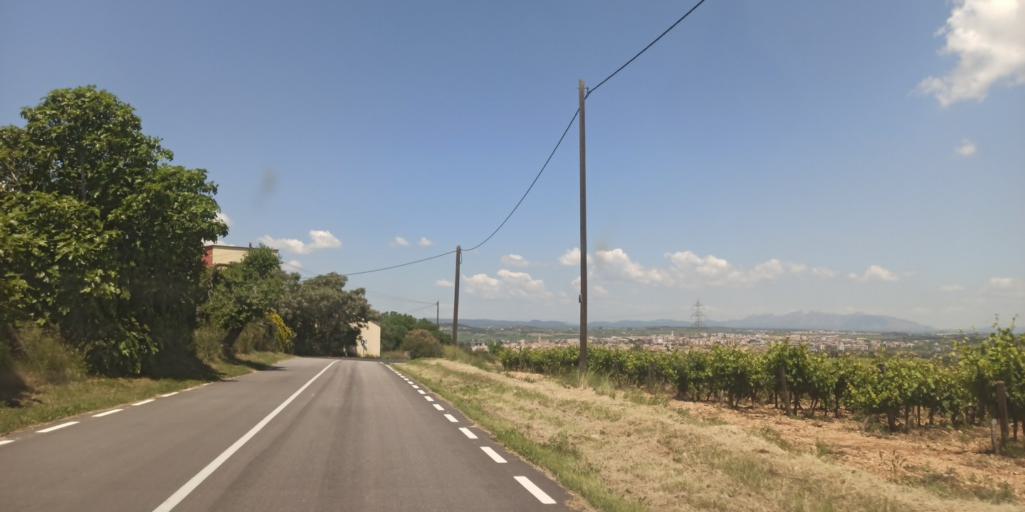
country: ES
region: Catalonia
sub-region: Provincia de Barcelona
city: Vilafranca del Penedes
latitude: 41.3115
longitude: 1.6915
